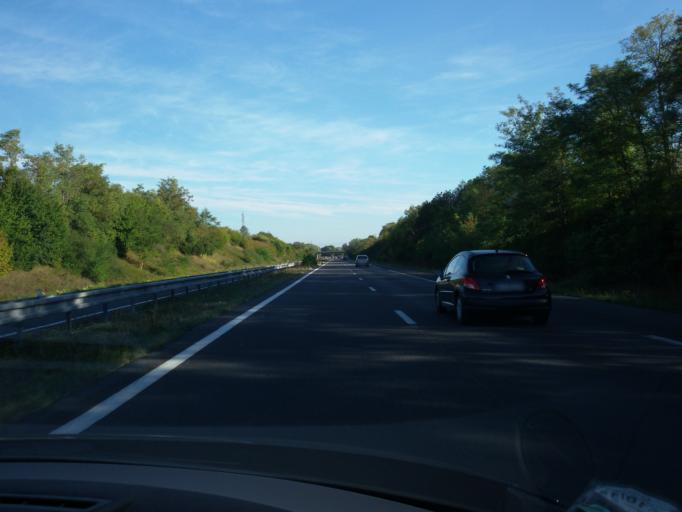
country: FR
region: Centre
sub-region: Departement du Cher
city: Foecy
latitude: 47.1582
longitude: 2.1833
